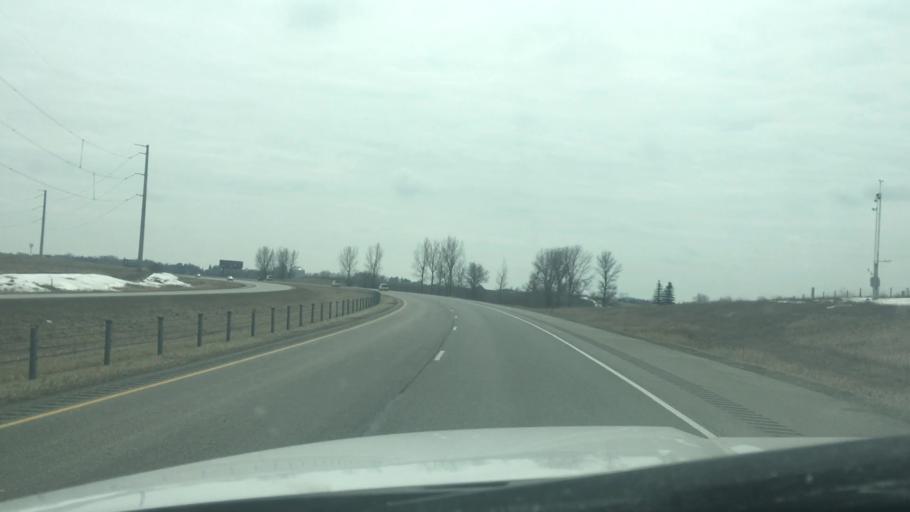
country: US
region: Minnesota
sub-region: Clay County
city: Barnesville
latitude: 46.4913
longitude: -96.2909
